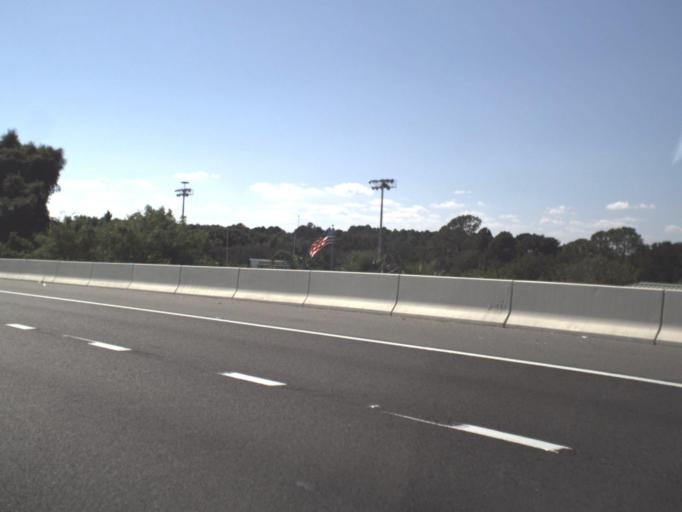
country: US
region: Florida
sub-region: Hillsborough County
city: Town 'n' Country
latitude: 27.9756
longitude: -82.5470
